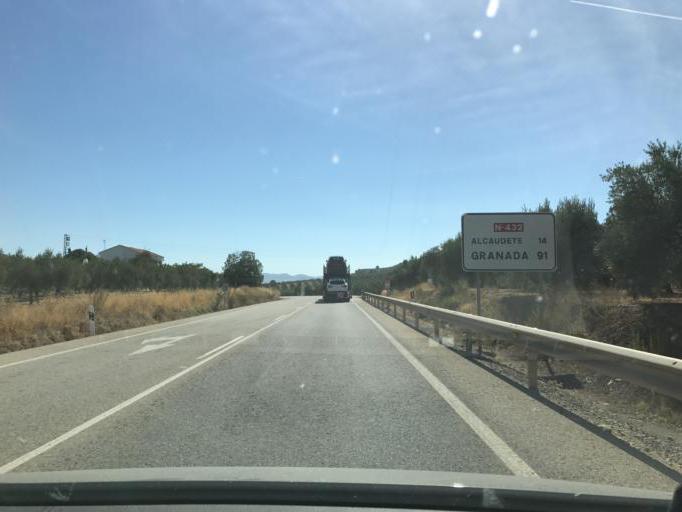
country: ES
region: Andalusia
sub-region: Province of Cordoba
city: Luque
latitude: 37.5652
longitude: -4.2262
